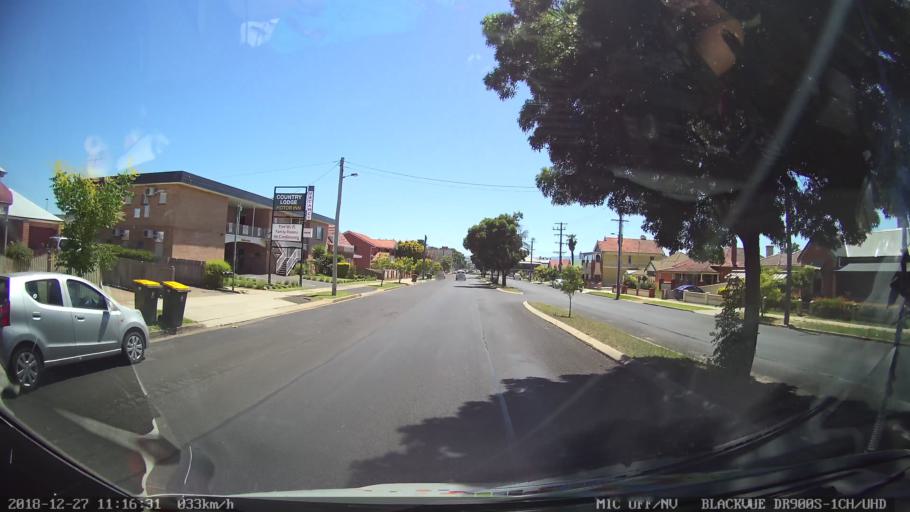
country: AU
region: New South Wales
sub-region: Bathurst Regional
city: Bathurst
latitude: -33.4216
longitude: 149.5744
